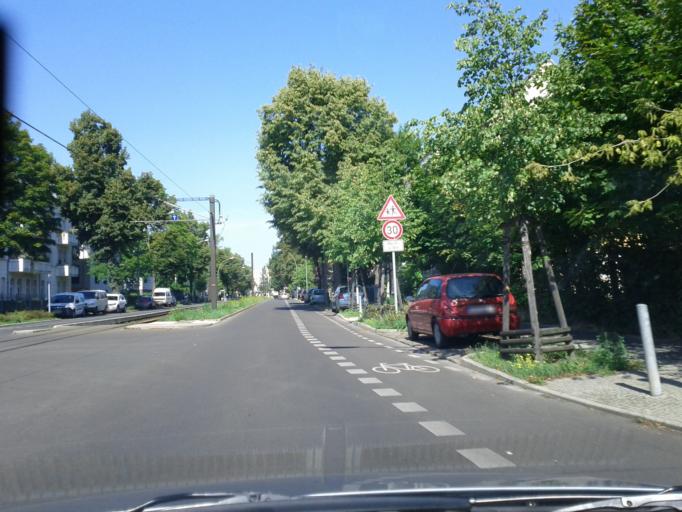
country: DE
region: Berlin
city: Niederschonhausen
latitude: 52.5809
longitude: 13.3955
